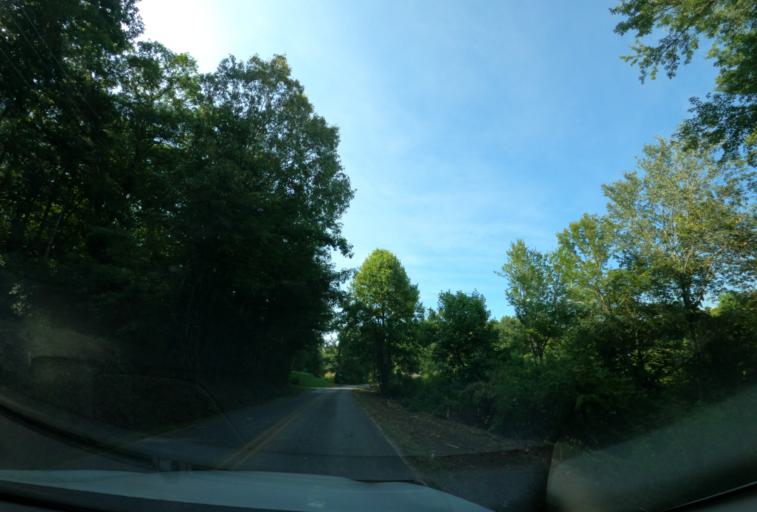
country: US
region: North Carolina
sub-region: Transylvania County
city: Brevard
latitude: 35.2644
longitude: -82.6792
